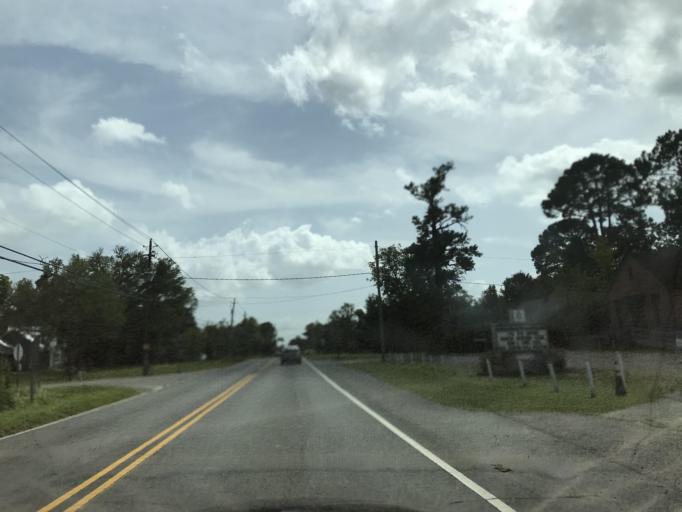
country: US
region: North Carolina
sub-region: New Hanover County
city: Wrightsboro
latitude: 34.2824
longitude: -77.9227
